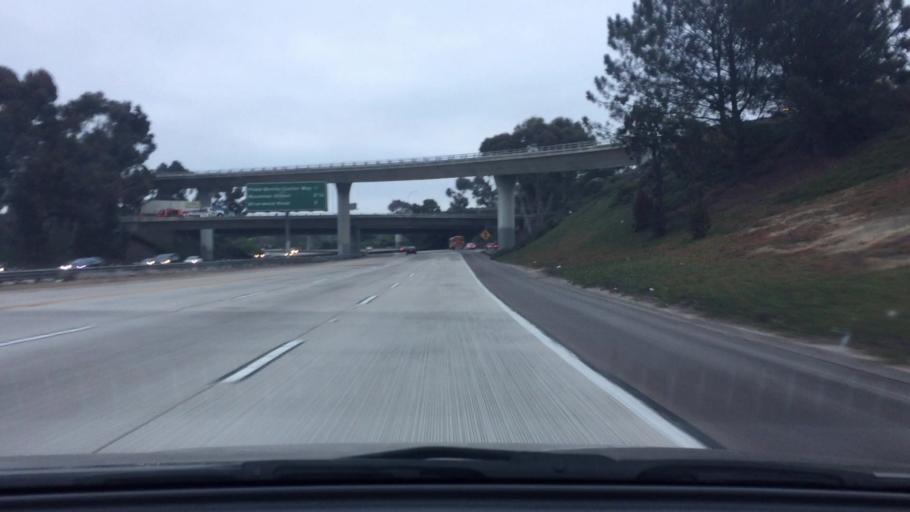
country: US
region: California
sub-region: San Diego County
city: Chula Vista
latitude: 32.6583
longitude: -117.0772
